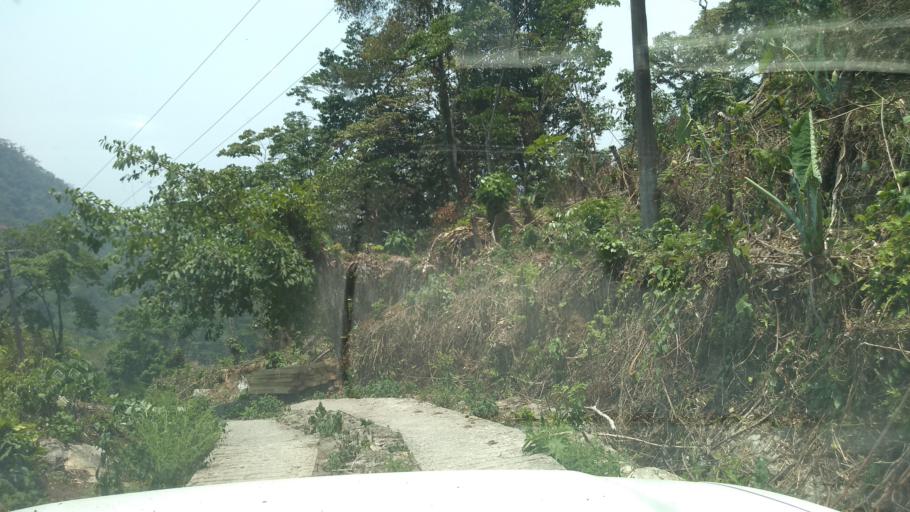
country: MX
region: Veracruz
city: Motzorongo
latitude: 18.6004
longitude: -96.7486
